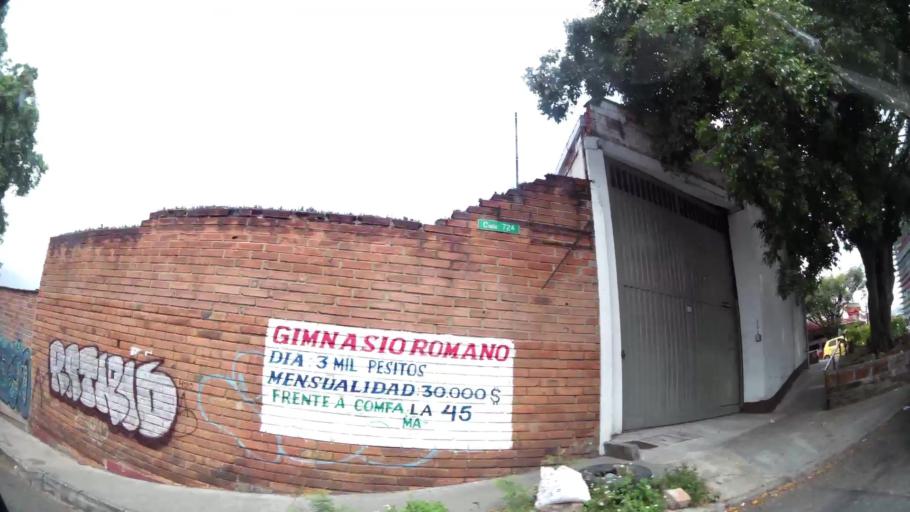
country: CO
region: Antioquia
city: Medellin
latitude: 6.2677
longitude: -75.5591
